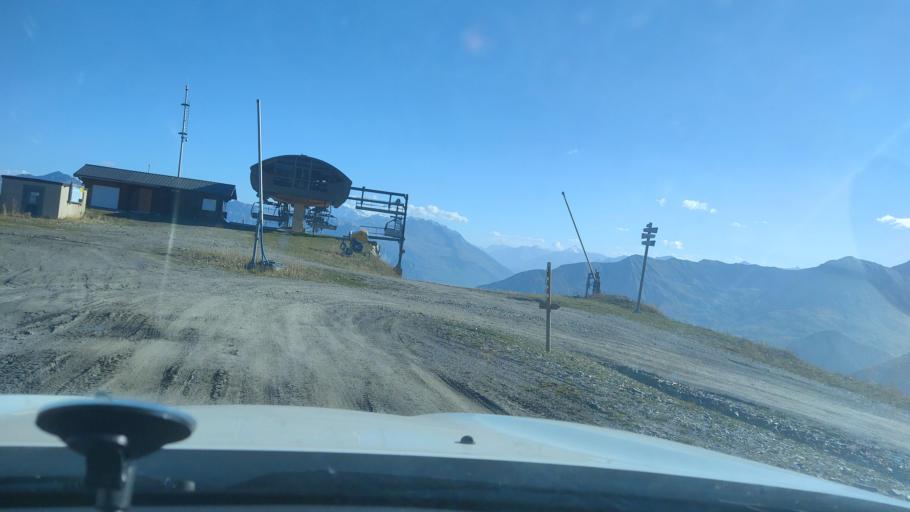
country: FR
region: Rhone-Alpes
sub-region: Departement de la Savoie
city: Saint-Etienne-de-Cuines
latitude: 45.2541
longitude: 6.2399
